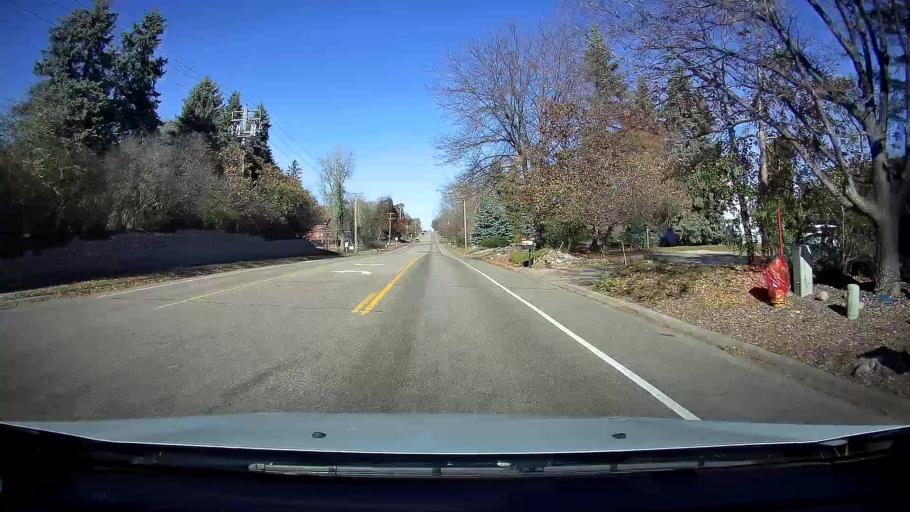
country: US
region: Minnesota
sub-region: Ramsey County
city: Shoreview
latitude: 45.0695
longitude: -93.1574
